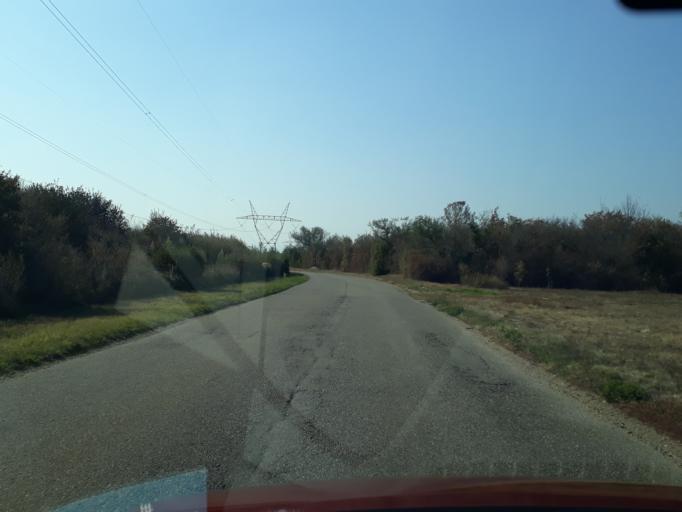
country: FR
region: Rhone-Alpes
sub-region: Departement du Rhone
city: Saint-Bonnet-de-Mure
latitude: 45.6794
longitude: 5.0165
